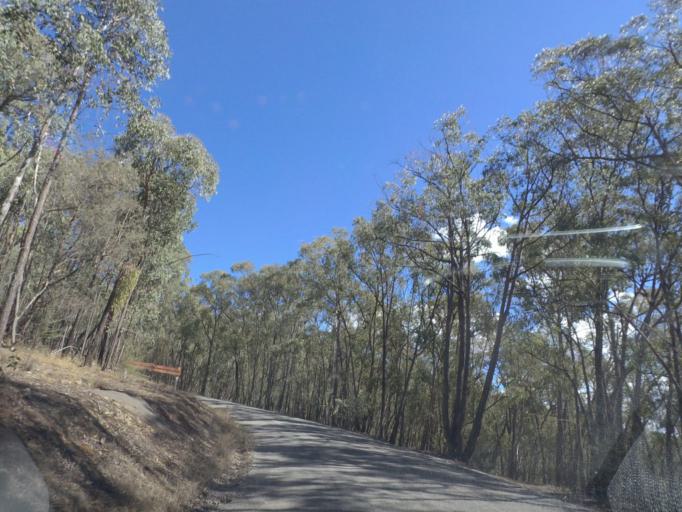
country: AU
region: Victoria
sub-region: Murrindindi
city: Alexandra
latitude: -37.3069
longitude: 145.8220
